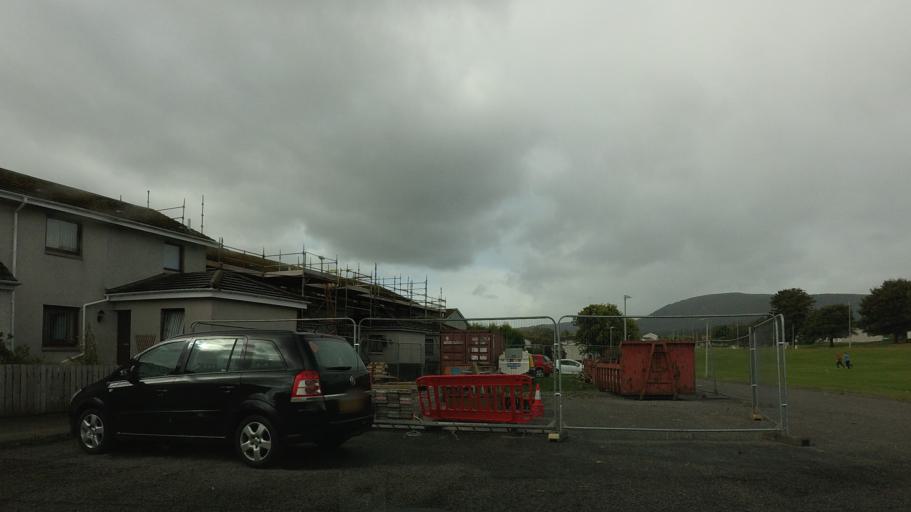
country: GB
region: Scotland
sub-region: Highland
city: Alness
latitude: 57.6947
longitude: -4.2726
